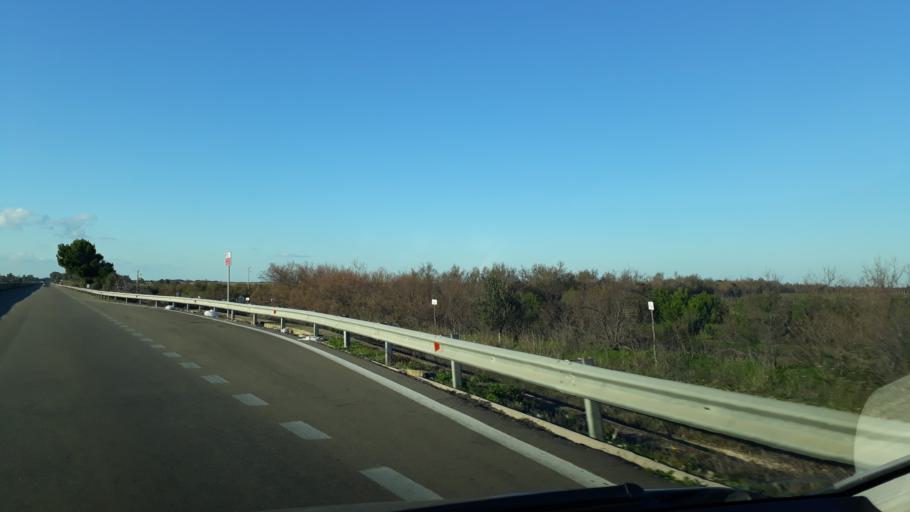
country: IT
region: Apulia
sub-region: Provincia di Brindisi
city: San Vito dei Normanni
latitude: 40.6971
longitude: 17.8111
